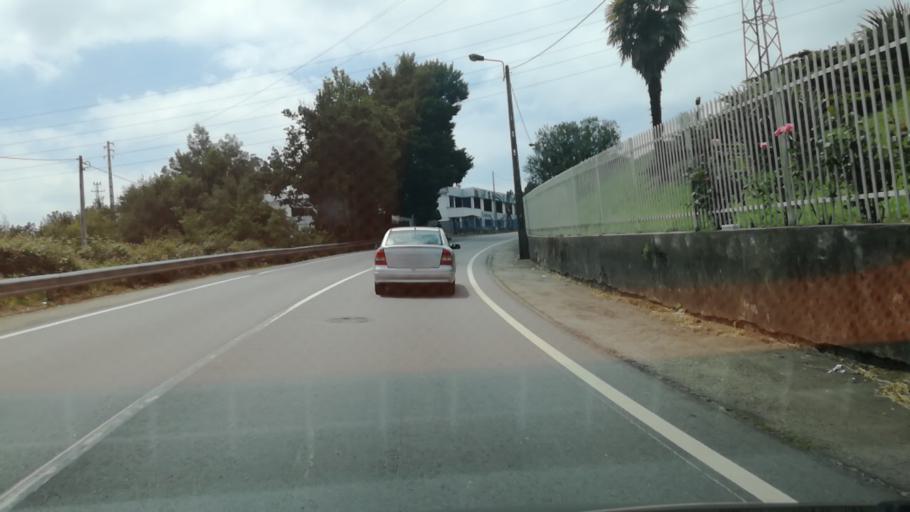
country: PT
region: Porto
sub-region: Trofa
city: Sao Romao do Coronado
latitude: 41.3096
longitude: -8.5808
